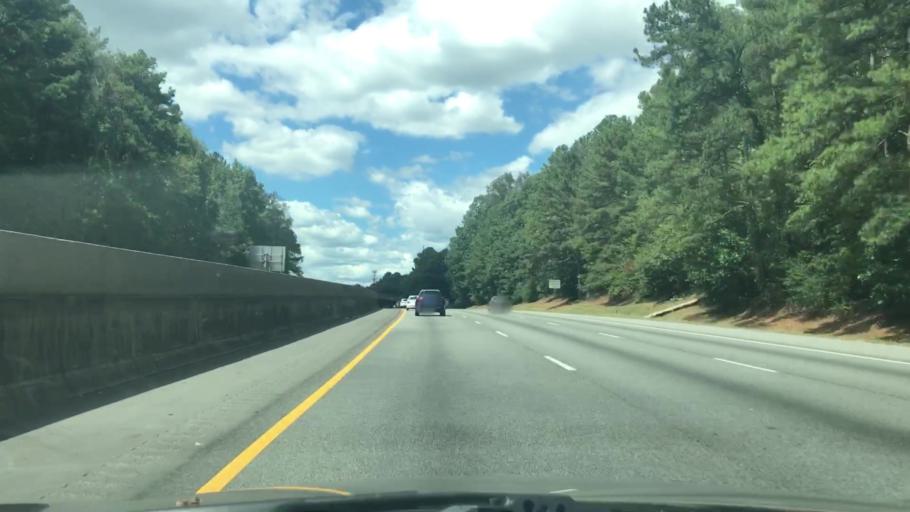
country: US
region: Georgia
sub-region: DeKalb County
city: Stone Mountain
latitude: 33.8266
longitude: -84.1753
